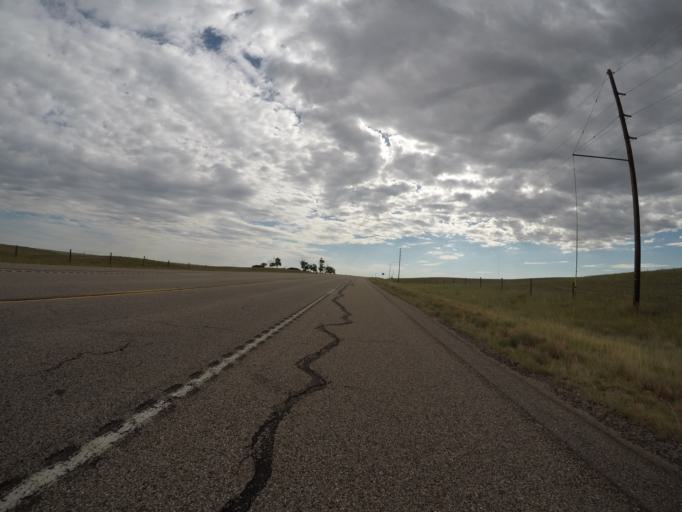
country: US
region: Wyoming
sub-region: Laramie County
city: Cheyenne
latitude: 41.1511
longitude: -104.9745
